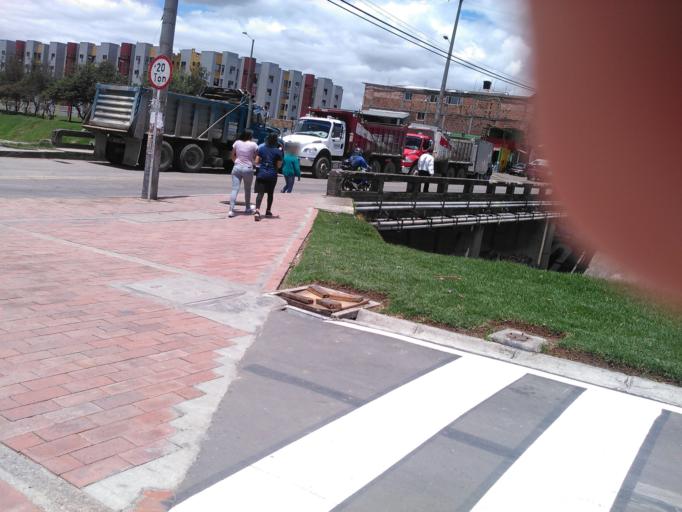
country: CO
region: Bogota D.C.
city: Bogota
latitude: 4.6181
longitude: -74.1248
